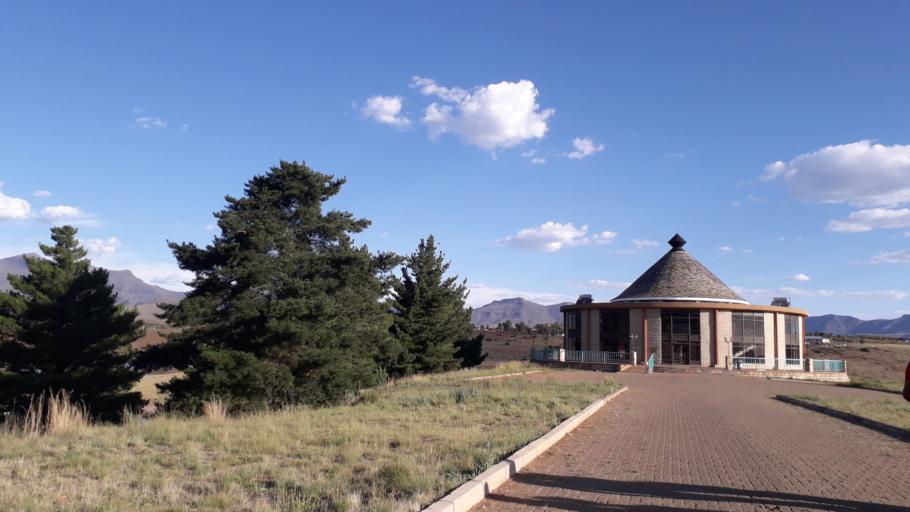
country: LS
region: Berea
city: Teyateyaneng
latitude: -29.3337
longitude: 27.7751
